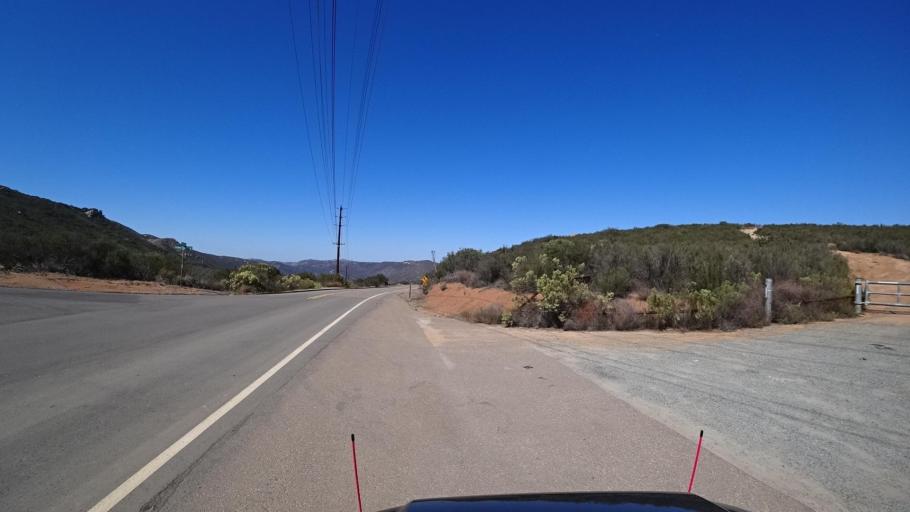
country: US
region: California
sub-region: San Diego County
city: Alpine
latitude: 32.7789
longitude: -116.7158
